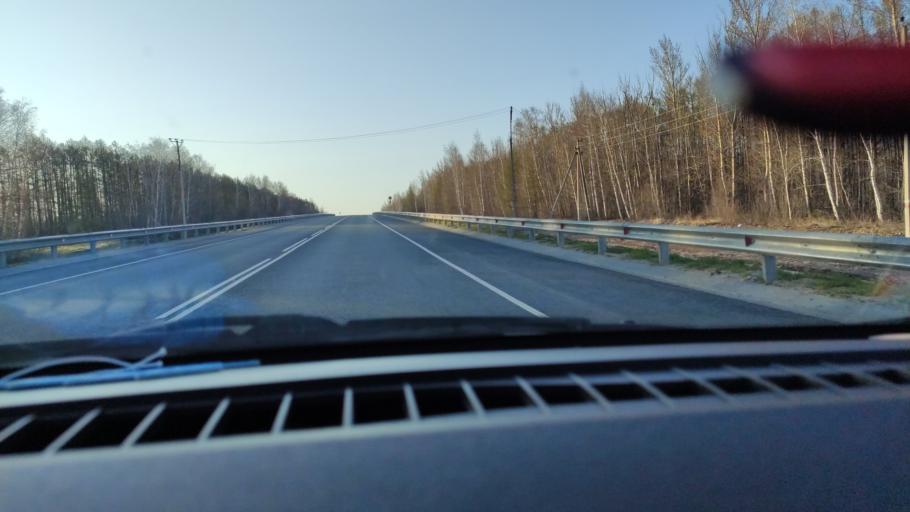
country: RU
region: Saratov
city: Shikhany
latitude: 52.1475
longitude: 47.1947
